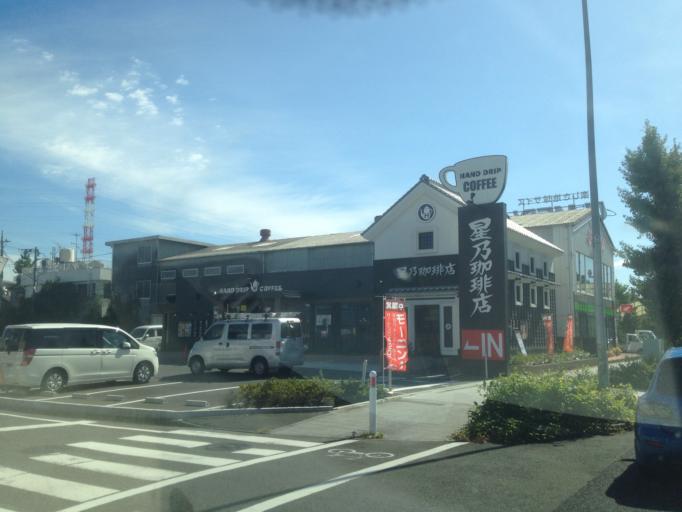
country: JP
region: Tokyo
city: Hachioji
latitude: 35.5796
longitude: 139.3604
